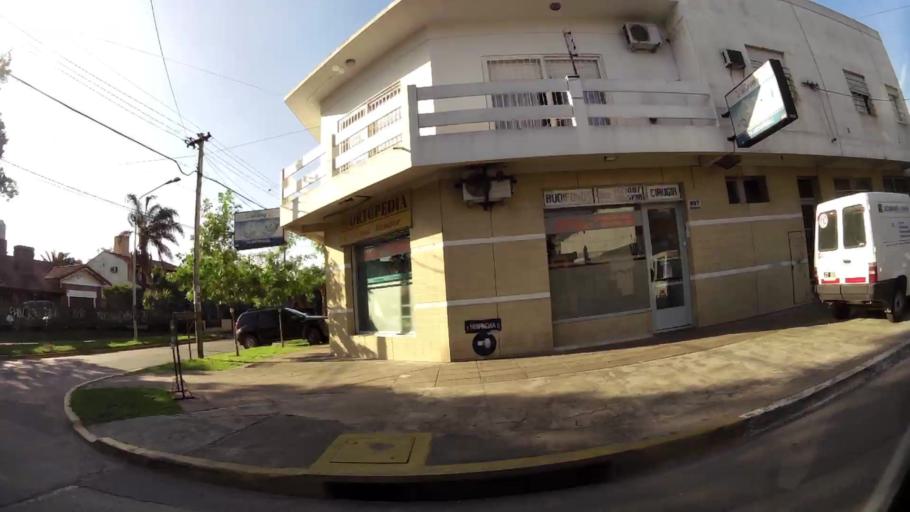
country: AR
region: Buenos Aires
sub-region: Partido de Merlo
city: Merlo
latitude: -34.6679
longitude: -58.7310
